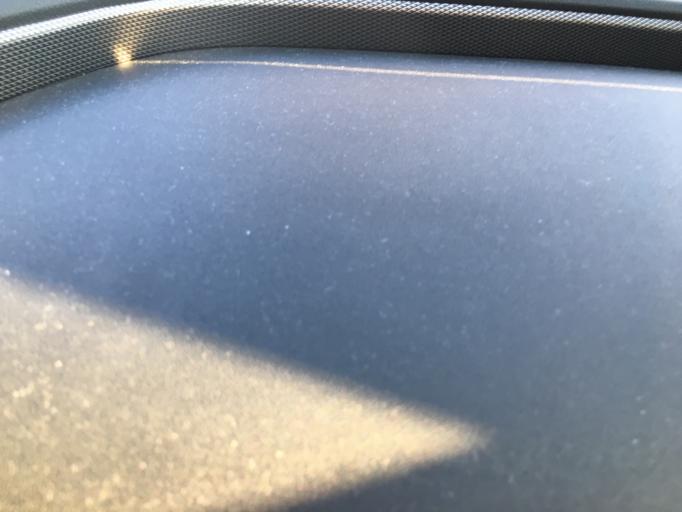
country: US
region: Connecticut
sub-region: Hartford County
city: Suffield Depot
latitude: 41.9732
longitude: -72.6543
